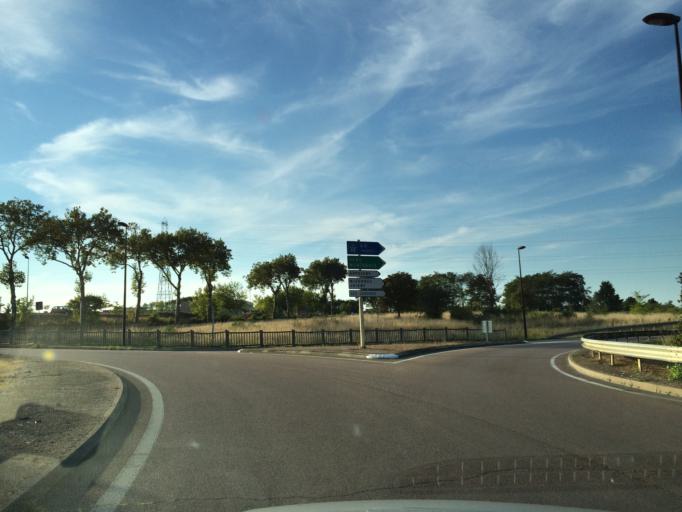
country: FR
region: Bourgogne
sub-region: Departement de l'Yonne
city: Auxerre
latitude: 47.8165
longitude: 3.5607
